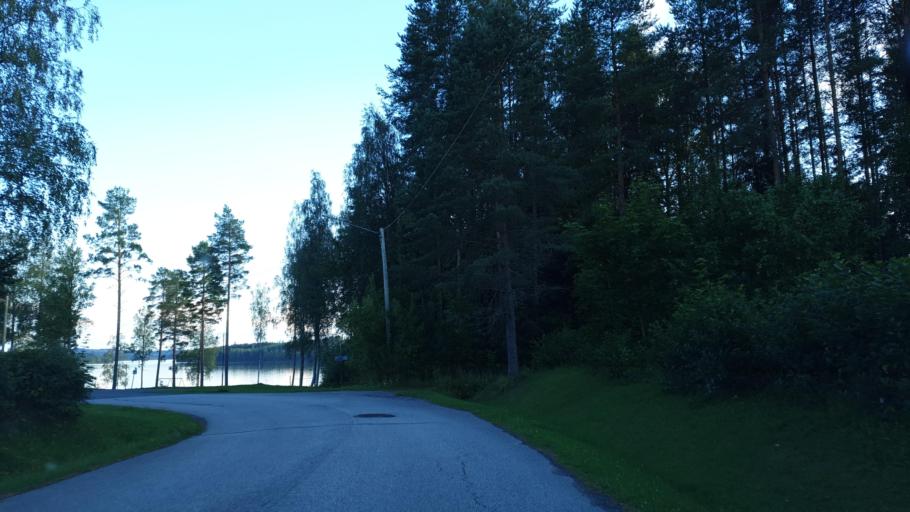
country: FI
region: Northern Savo
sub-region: Koillis-Savo
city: Kaavi
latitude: 62.9754
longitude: 28.4680
